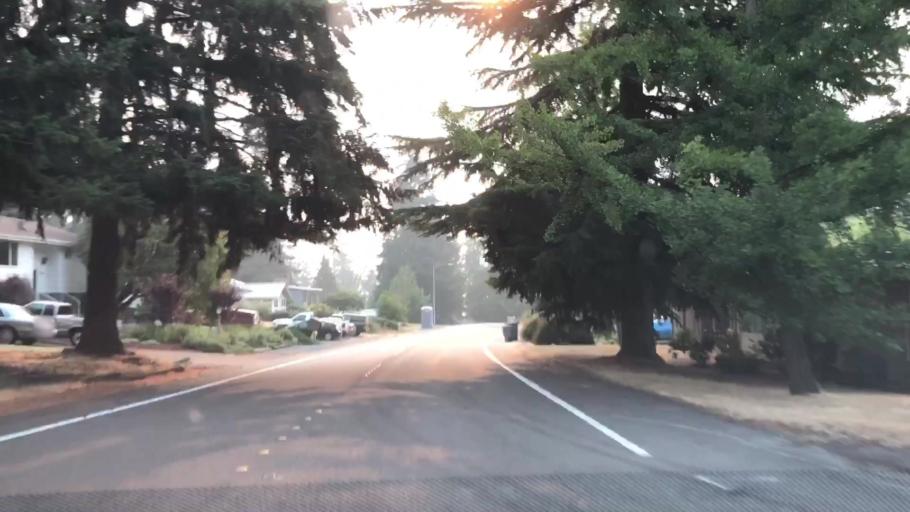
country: US
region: Washington
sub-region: King County
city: Newport
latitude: 47.5861
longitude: -122.1718
